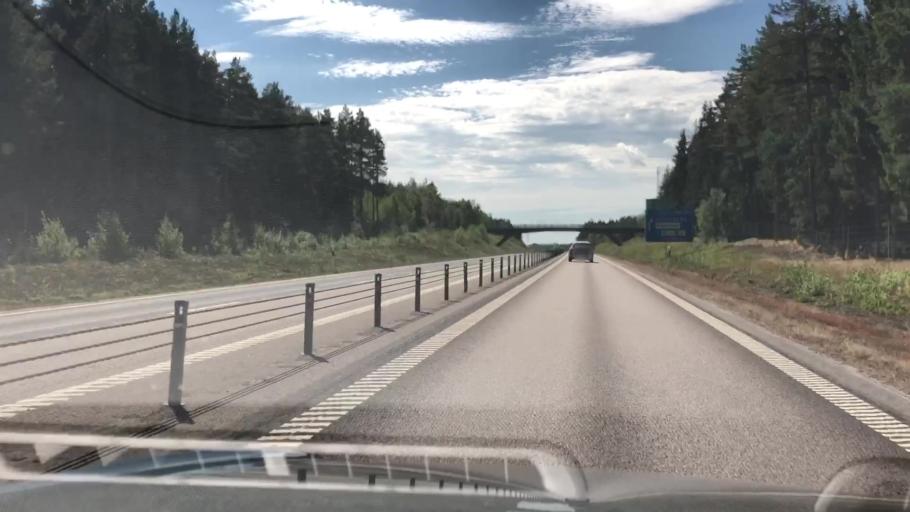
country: SE
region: Kalmar
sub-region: Torsas Kommun
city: Torsas
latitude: 56.4659
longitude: 16.0787
